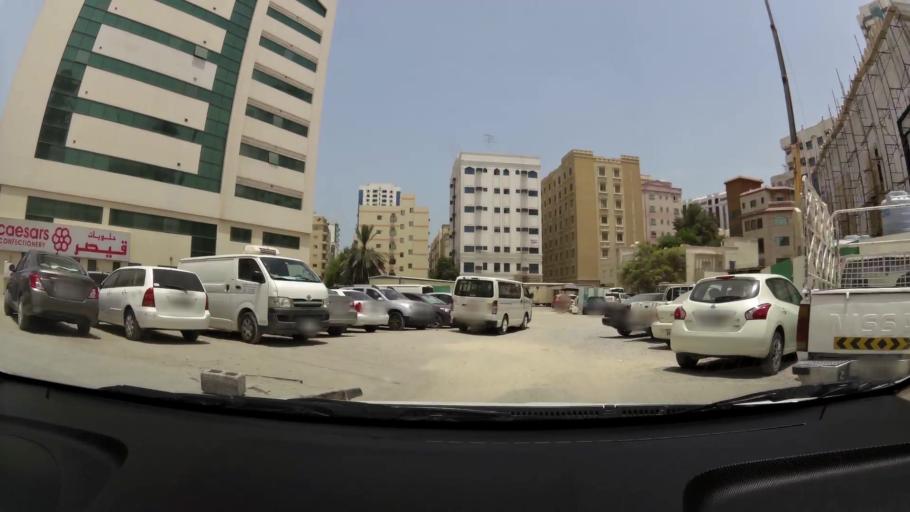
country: AE
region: Ash Shariqah
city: Sharjah
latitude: 25.3526
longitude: 55.3898
